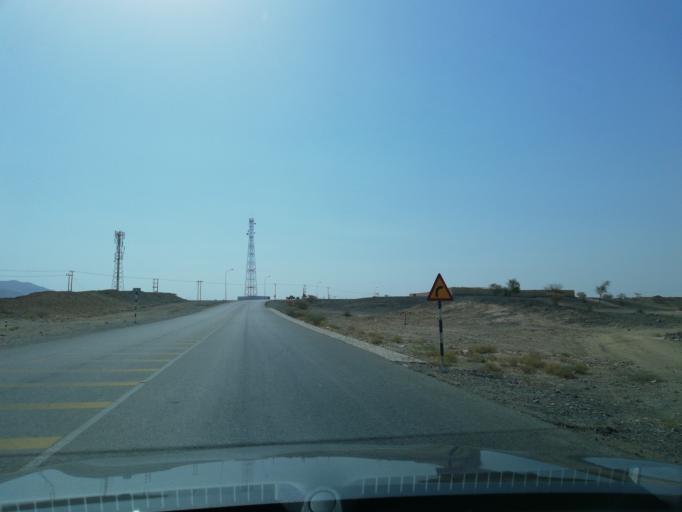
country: OM
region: Muhafazat ad Dakhiliyah
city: Adam
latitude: 22.3670
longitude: 58.0591
